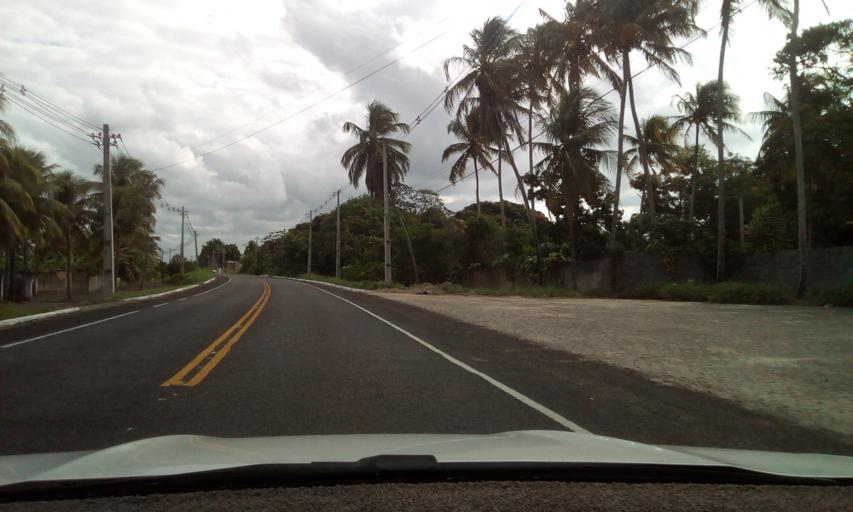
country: BR
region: Paraiba
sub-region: Rio Tinto
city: Rio Tinto
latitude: -6.8135
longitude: -35.0921
